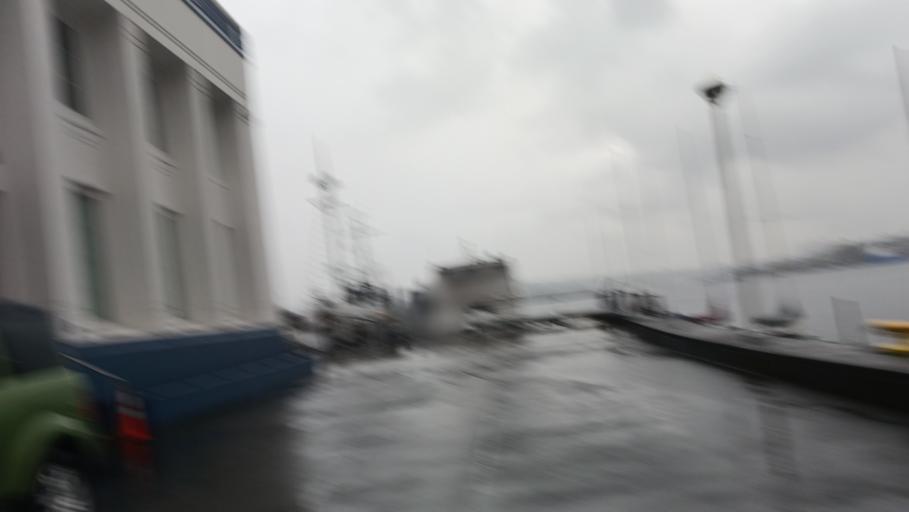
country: US
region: Washington
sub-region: King County
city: Seattle
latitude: 47.6277
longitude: -122.3362
